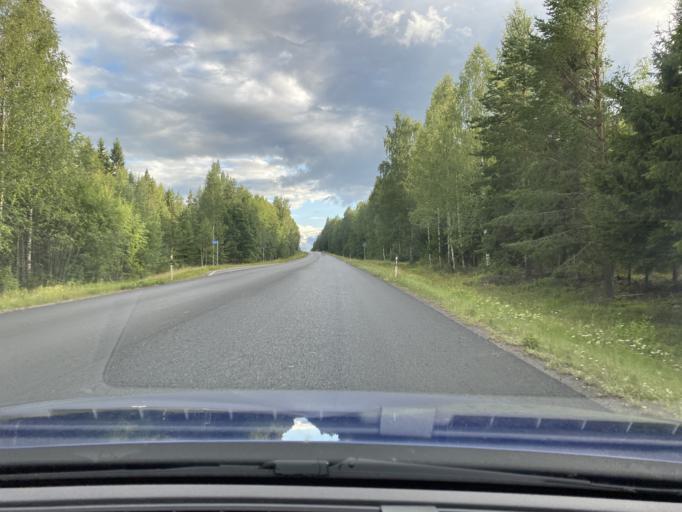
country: FI
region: Haeme
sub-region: Haemeenlinna
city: Renko
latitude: 60.9233
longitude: 24.3391
